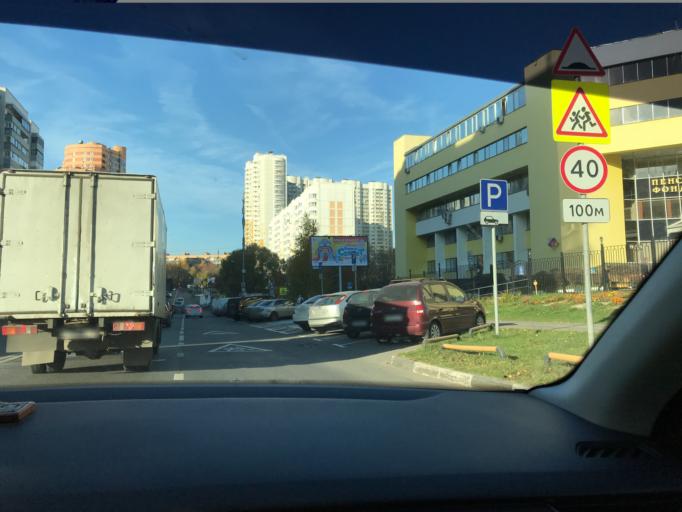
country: RU
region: Moscow
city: Khimki
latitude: 55.8835
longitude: 37.4285
